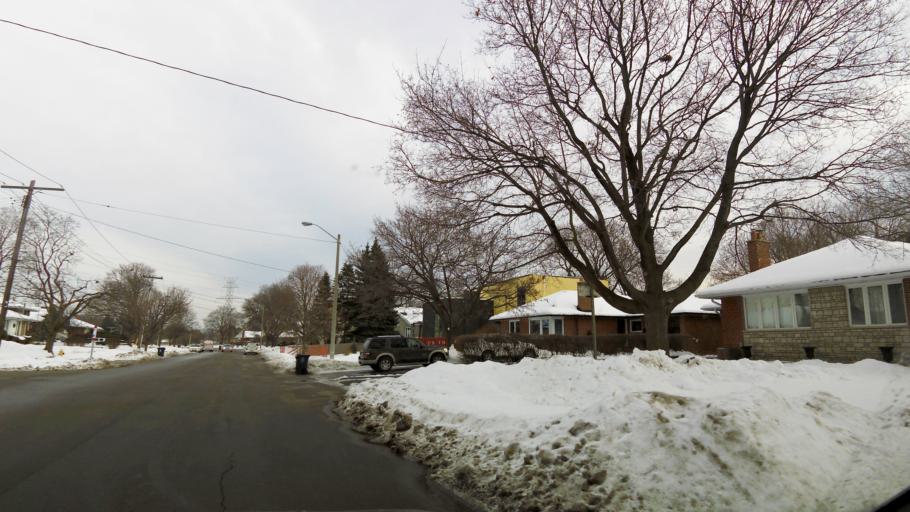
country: CA
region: Ontario
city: Etobicoke
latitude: 43.6664
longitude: -79.5574
